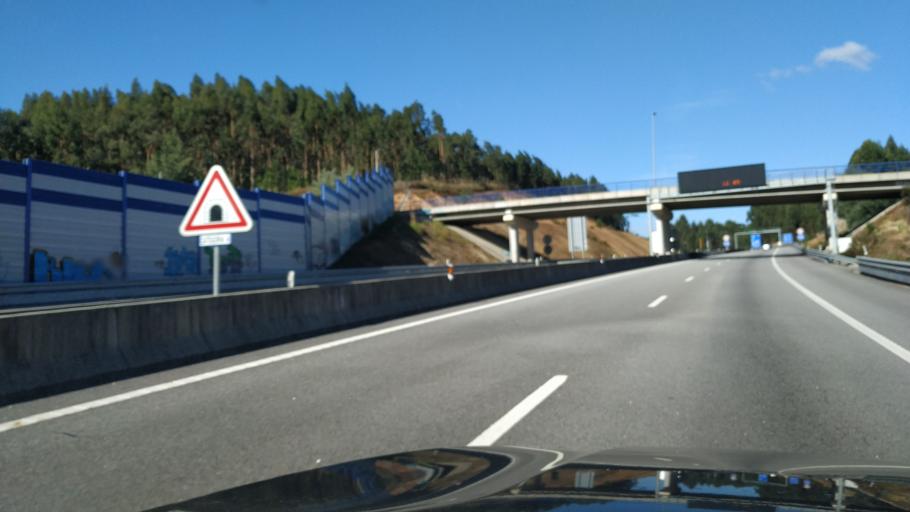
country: PT
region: Porto
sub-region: Vila Nova de Gaia
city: Sandim
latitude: 41.0499
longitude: -8.5089
